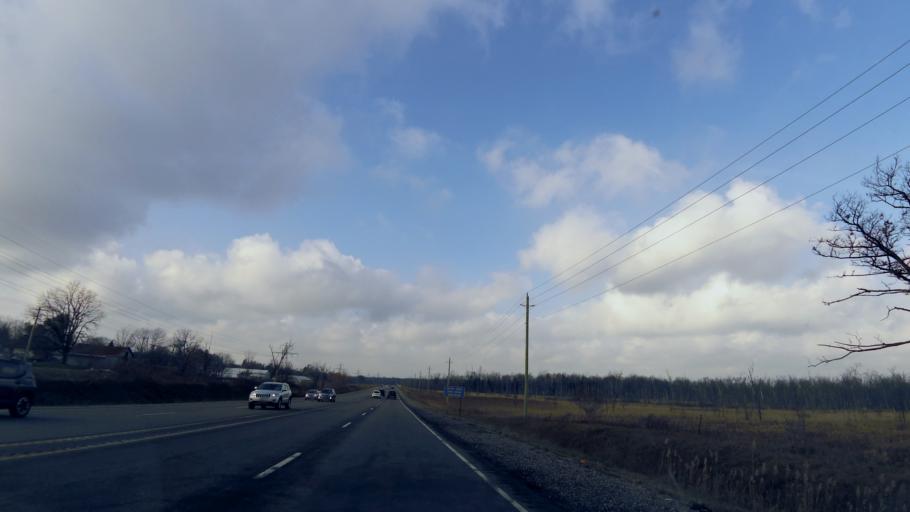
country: CA
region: Ontario
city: Ancaster
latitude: 43.4031
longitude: -80.0399
